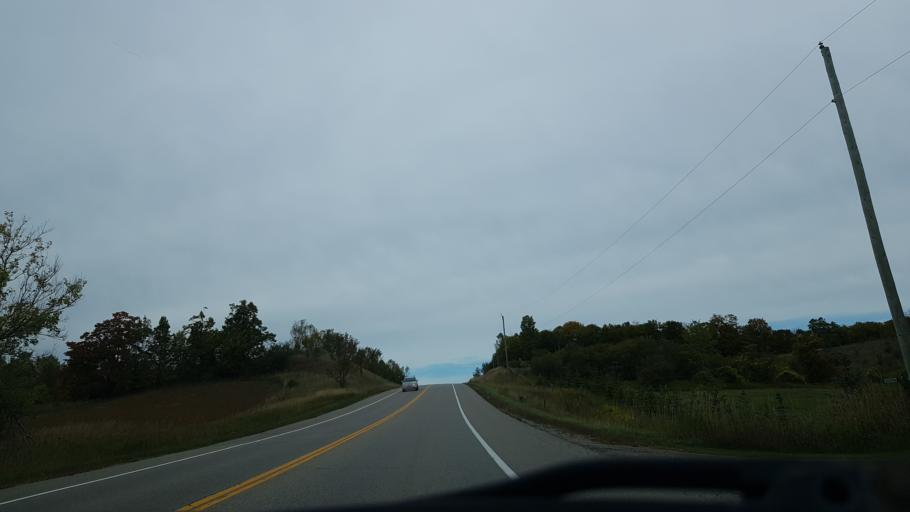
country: CA
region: Ontario
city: Orangeville
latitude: 44.0551
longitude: -80.0126
